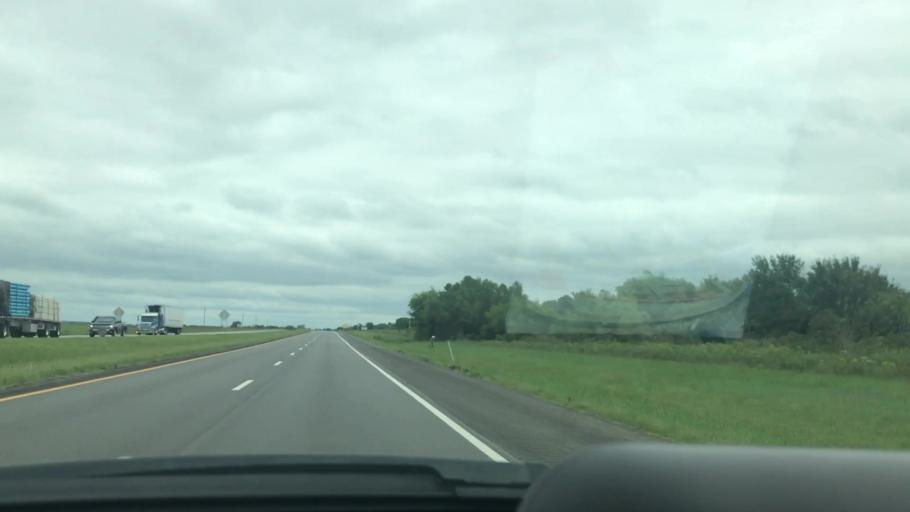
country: US
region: Oklahoma
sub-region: Mayes County
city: Pryor
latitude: 36.4491
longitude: -95.2668
